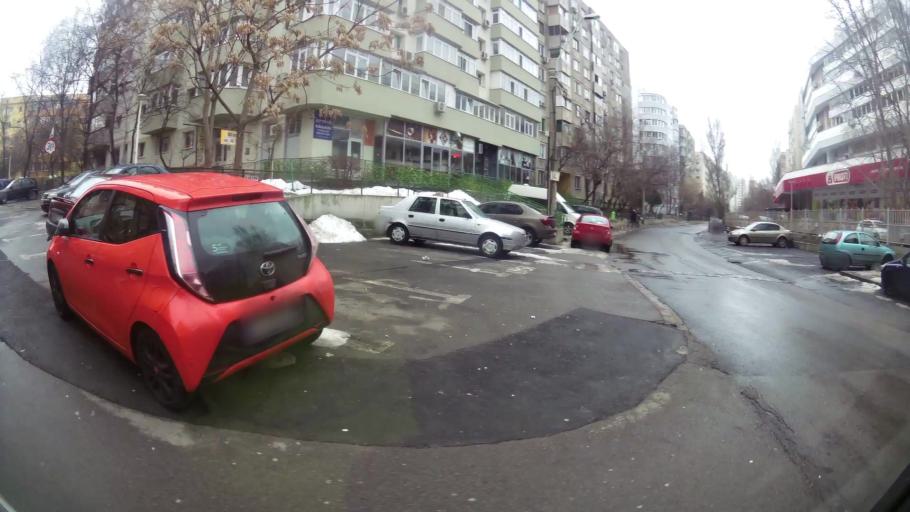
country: RO
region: Bucuresti
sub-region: Municipiul Bucuresti
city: Bucharest
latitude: 44.4129
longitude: 26.1386
